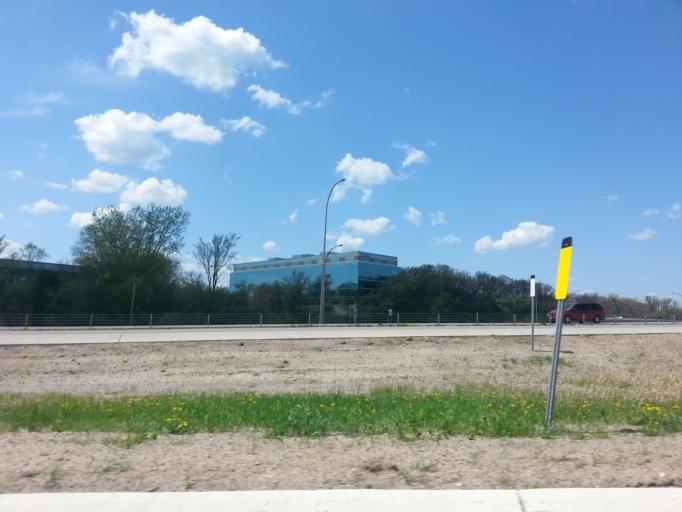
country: US
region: Minnesota
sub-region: Hennepin County
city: Edina
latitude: 44.8880
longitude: -93.3991
